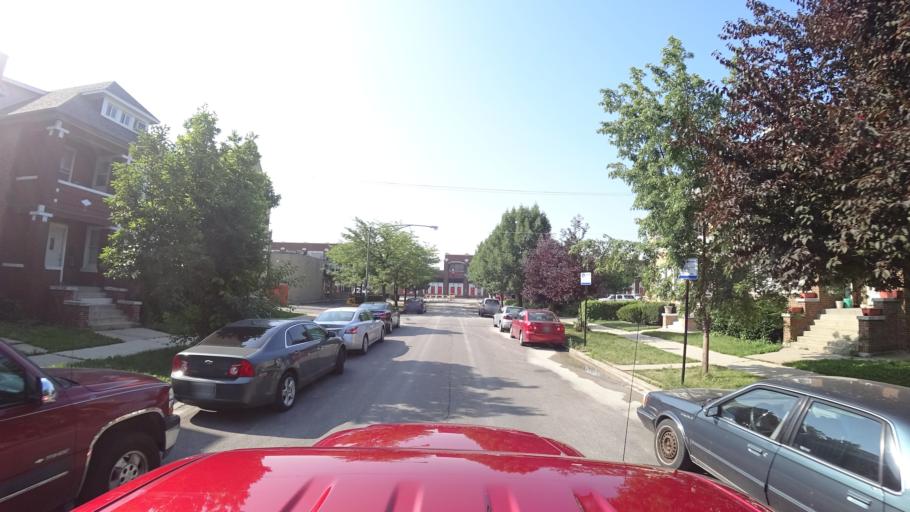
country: US
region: Illinois
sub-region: Cook County
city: Cicero
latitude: 41.8088
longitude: -87.7087
